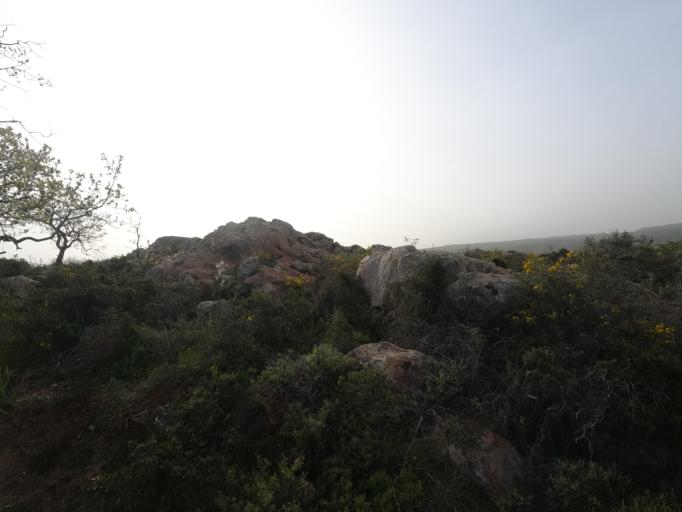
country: CY
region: Pafos
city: Pegeia
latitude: 34.9566
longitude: 32.3804
